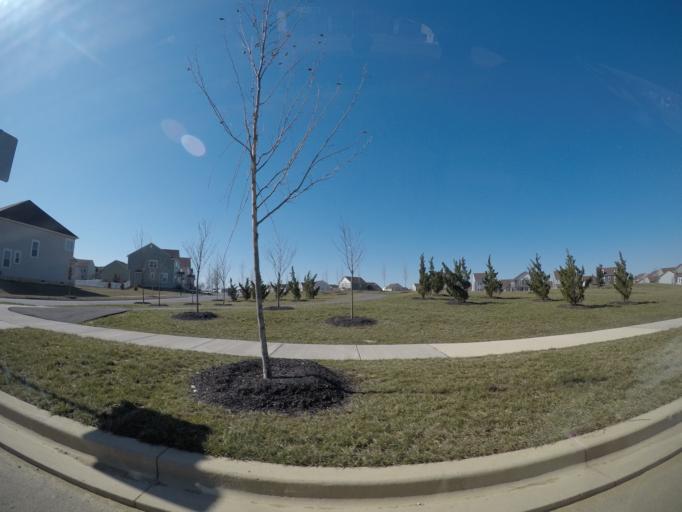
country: US
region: Delaware
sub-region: New Castle County
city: Middletown
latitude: 39.5144
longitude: -75.6663
